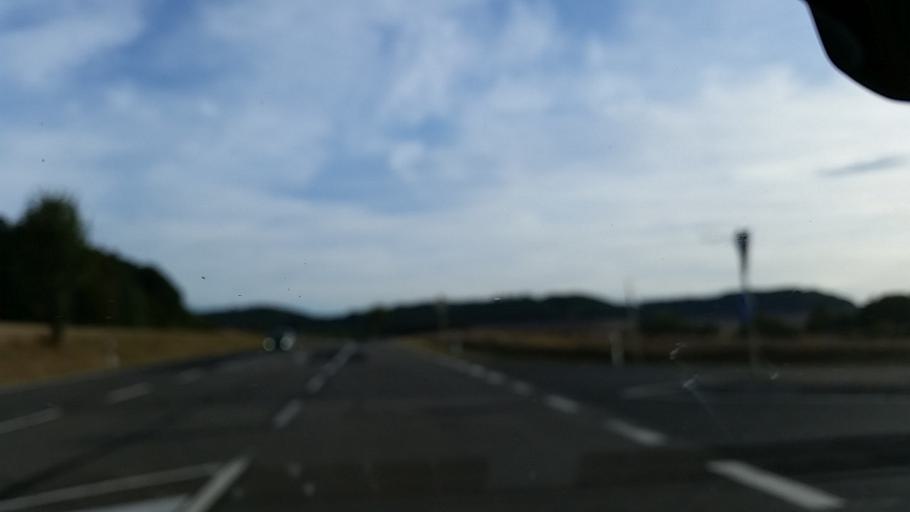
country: DE
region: Thuringia
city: Henneberg
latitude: 50.5056
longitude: 10.3563
